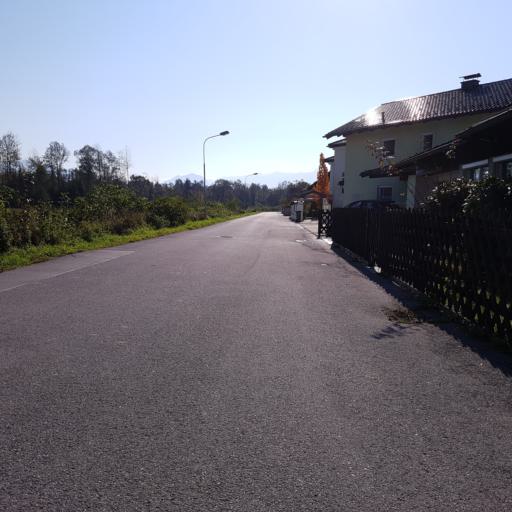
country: AT
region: Salzburg
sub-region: Politischer Bezirk Hallein
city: Puch bei Hallein
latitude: 47.7129
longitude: 13.0767
